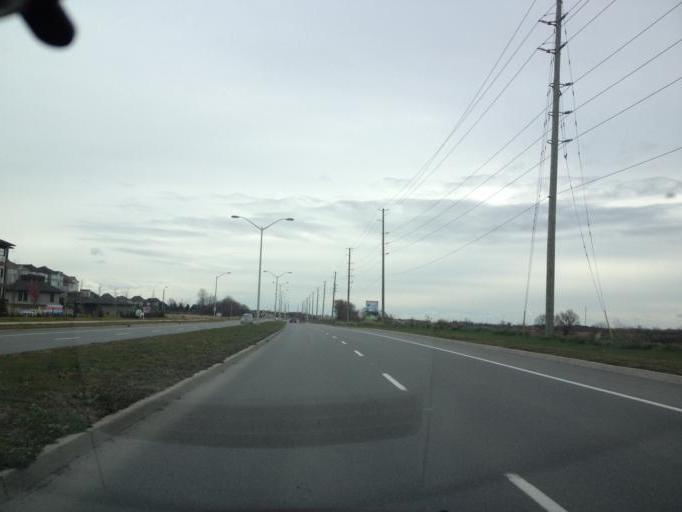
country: CA
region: Ontario
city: Bells Corners
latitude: 45.3133
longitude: -75.9371
